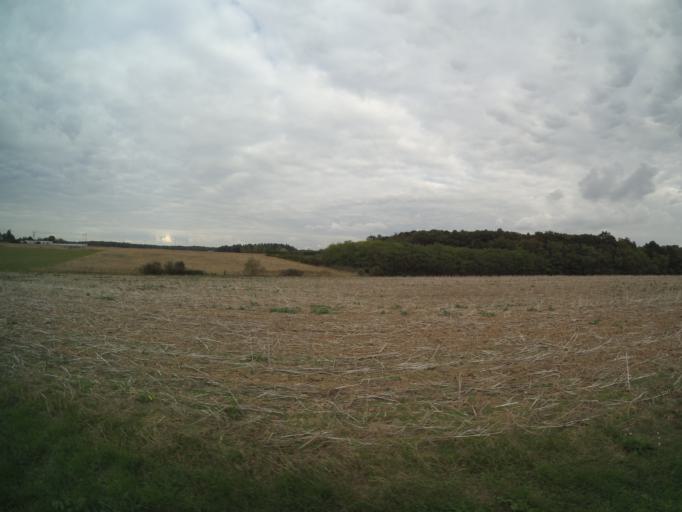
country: FR
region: Centre
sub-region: Departement d'Indre-et-Loire
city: Poce-sur-Cisse
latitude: 47.4984
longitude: 0.9752
